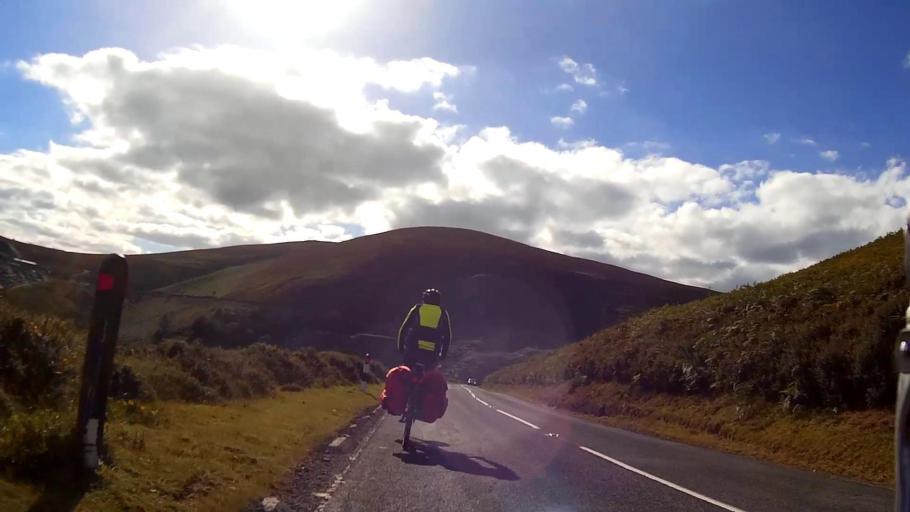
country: GB
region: Wales
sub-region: Denbighshire
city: Llandegla
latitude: 53.0147
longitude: -3.2104
